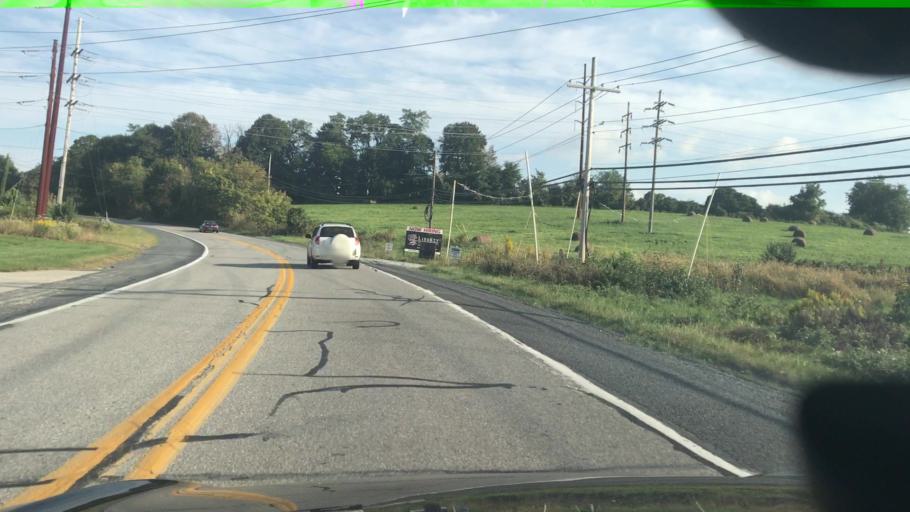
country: US
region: Pennsylvania
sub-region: Cumberland County
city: Shiremanstown
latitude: 40.2084
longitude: -76.9417
